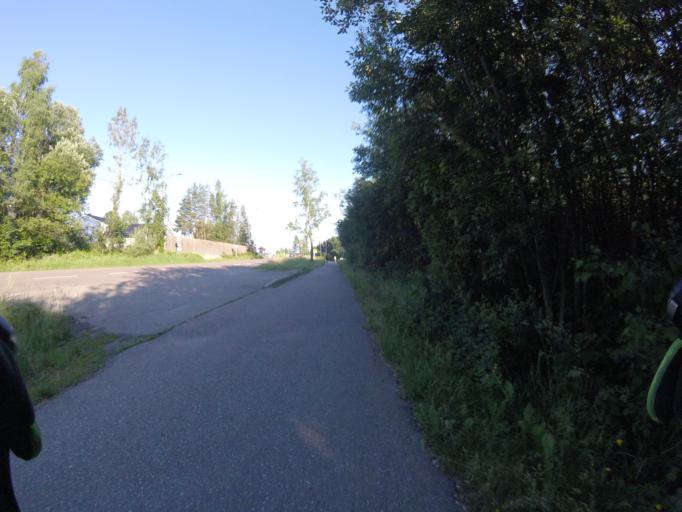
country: NO
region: Akershus
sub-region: Skedsmo
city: Lillestrom
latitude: 59.9643
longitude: 11.0572
